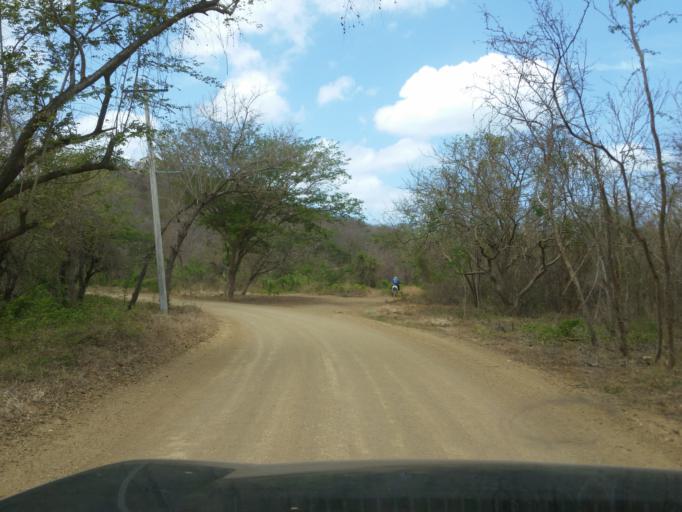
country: NI
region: Rivas
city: Tola
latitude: 11.4410
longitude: -86.0795
